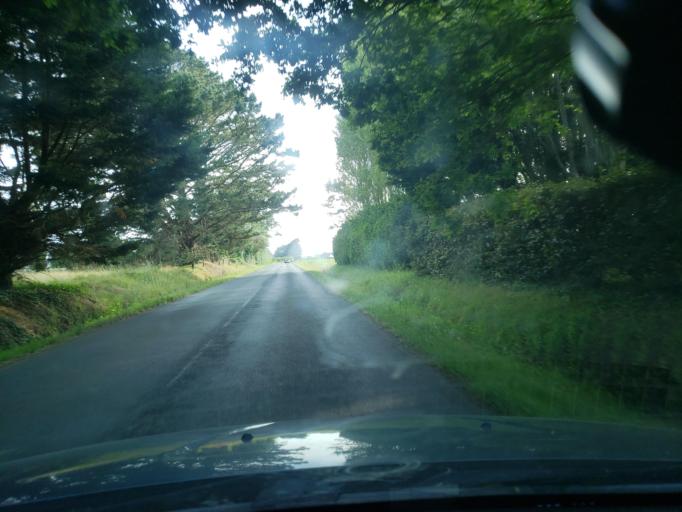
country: FR
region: Brittany
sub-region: Departement du Finistere
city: Treffiagat
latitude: 47.8104
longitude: -4.2498
